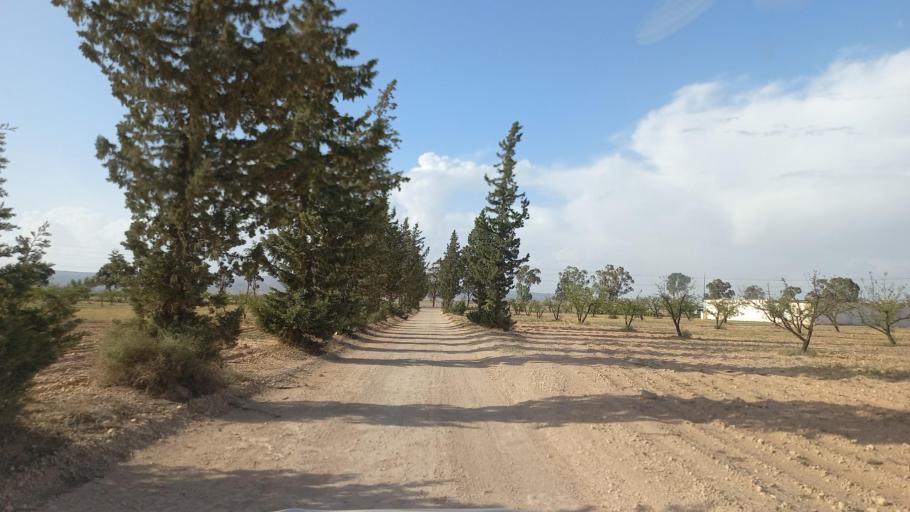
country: TN
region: Al Qasrayn
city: Kasserine
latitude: 35.2305
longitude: 8.9666
